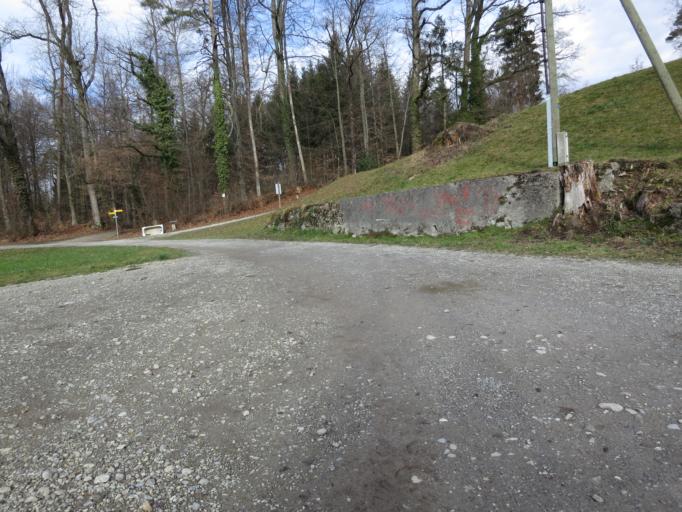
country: CH
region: Zurich
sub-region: Bezirk Meilen
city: Hombrechtikon
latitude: 47.2390
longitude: 8.7739
